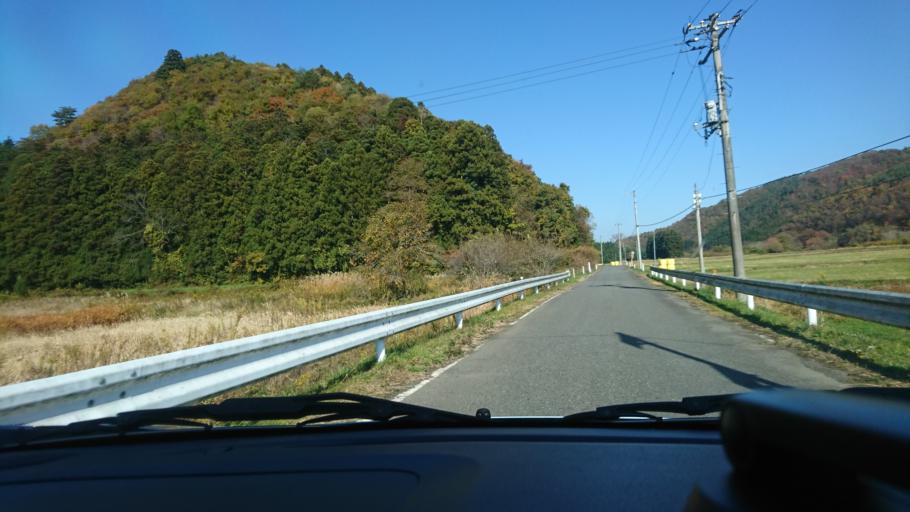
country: JP
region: Iwate
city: Ichinoseki
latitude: 38.8111
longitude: 141.2477
